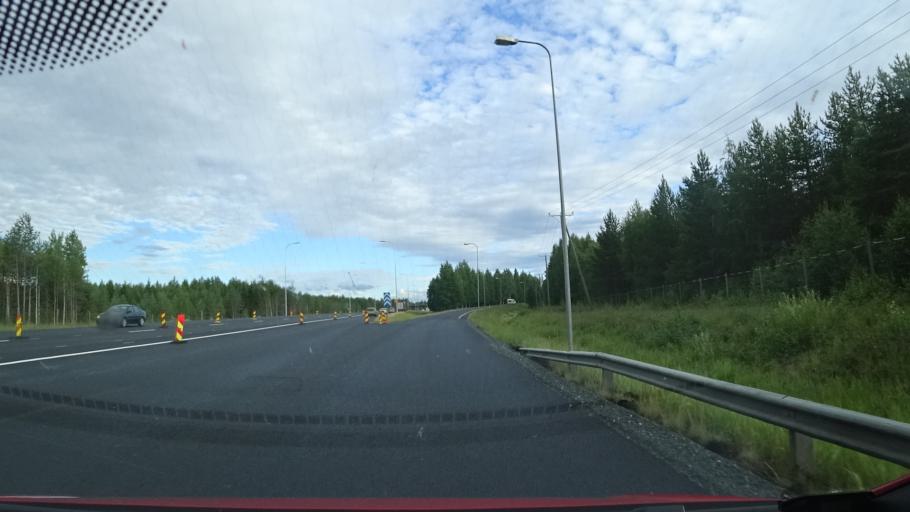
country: FI
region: Northern Ostrobothnia
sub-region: Oulu
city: Haukipudas
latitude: 65.2050
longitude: 25.4187
